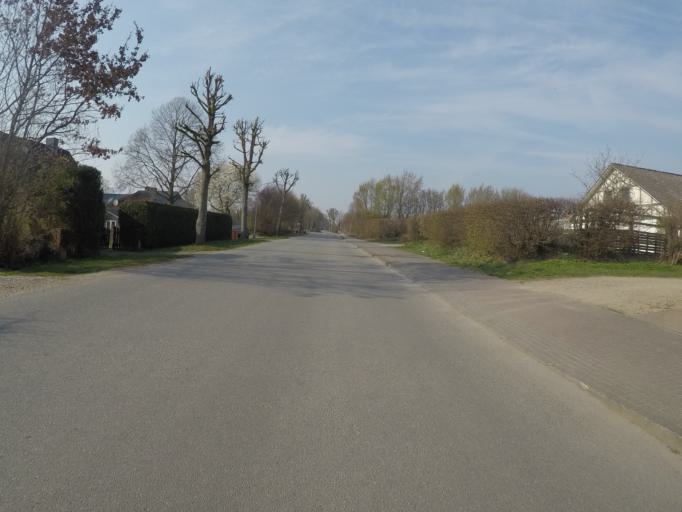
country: DE
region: Schleswig-Holstein
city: Kukels
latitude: 53.9024
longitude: 10.2322
